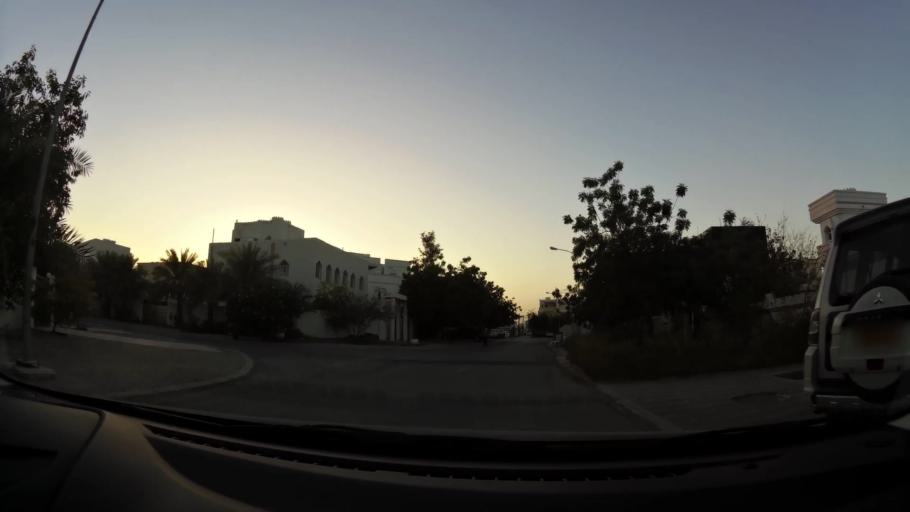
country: OM
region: Muhafazat Masqat
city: As Sib al Jadidah
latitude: 23.5933
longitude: 58.2292
